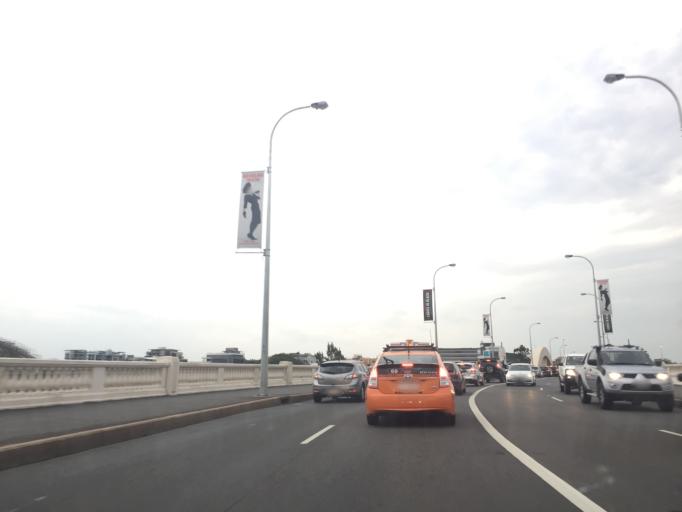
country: AU
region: Queensland
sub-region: Brisbane
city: South Brisbane
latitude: -27.4705
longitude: 153.0160
